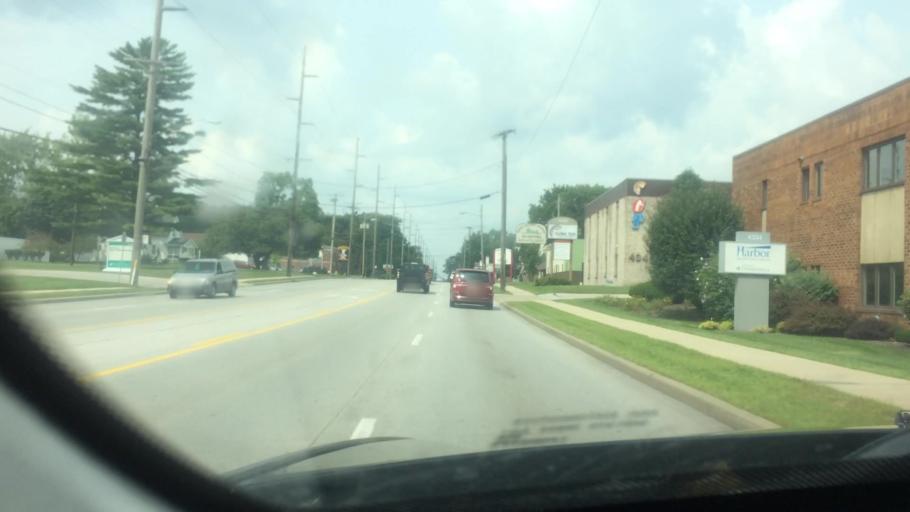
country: US
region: Ohio
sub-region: Lucas County
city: Ottawa Hills
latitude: 41.6968
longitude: -83.6233
